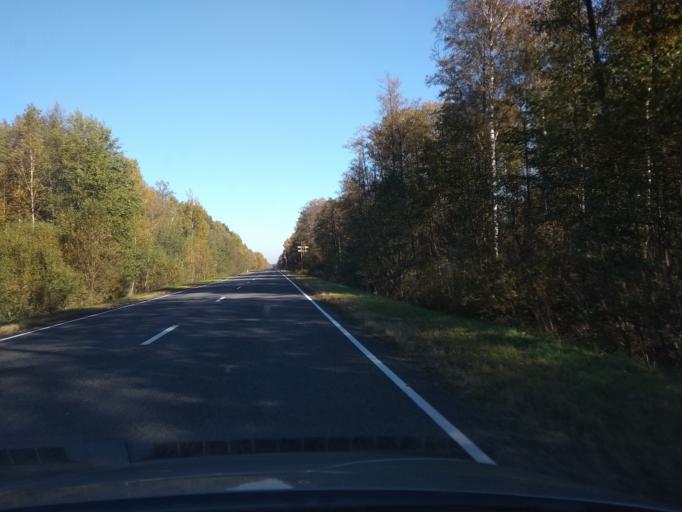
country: BY
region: Brest
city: Malaryta
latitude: 51.9412
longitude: 24.1761
